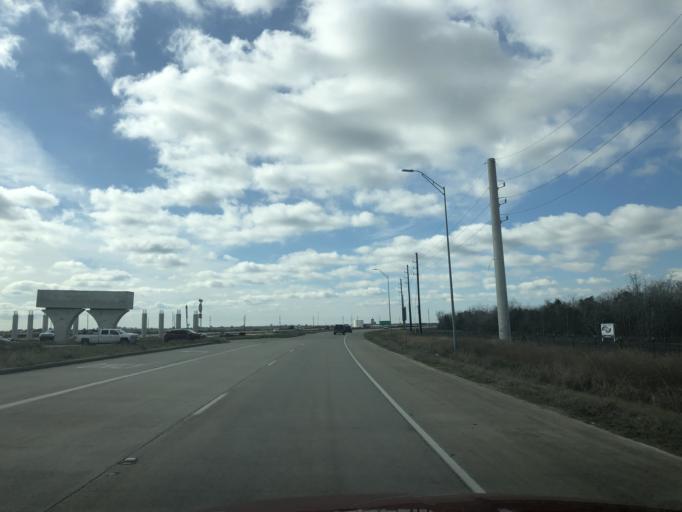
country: US
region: Texas
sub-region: Chambers County
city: Beach City
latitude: 29.7330
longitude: -94.8765
